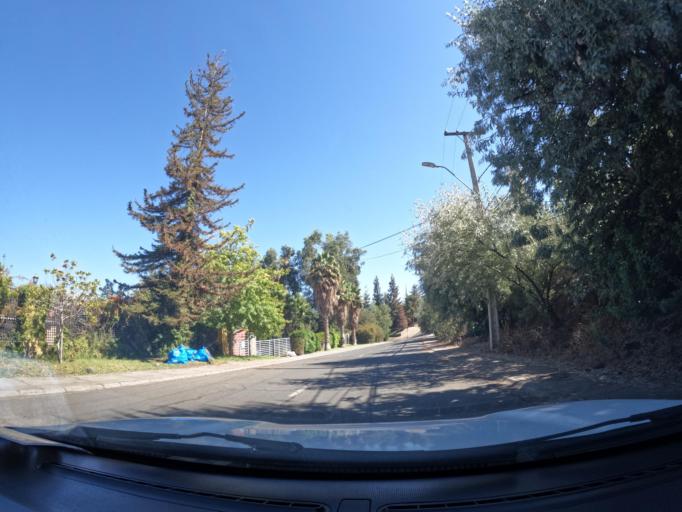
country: CL
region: Santiago Metropolitan
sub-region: Provincia de Santiago
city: Villa Presidente Frei, Nunoa, Santiago, Chile
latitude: -33.4780
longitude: -70.5186
